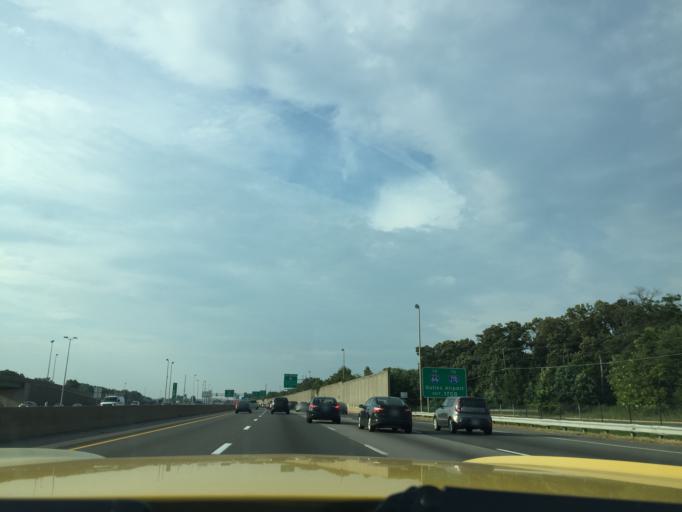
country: US
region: Virginia
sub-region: Fairfax County
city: Newington
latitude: 38.7550
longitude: -77.1836
